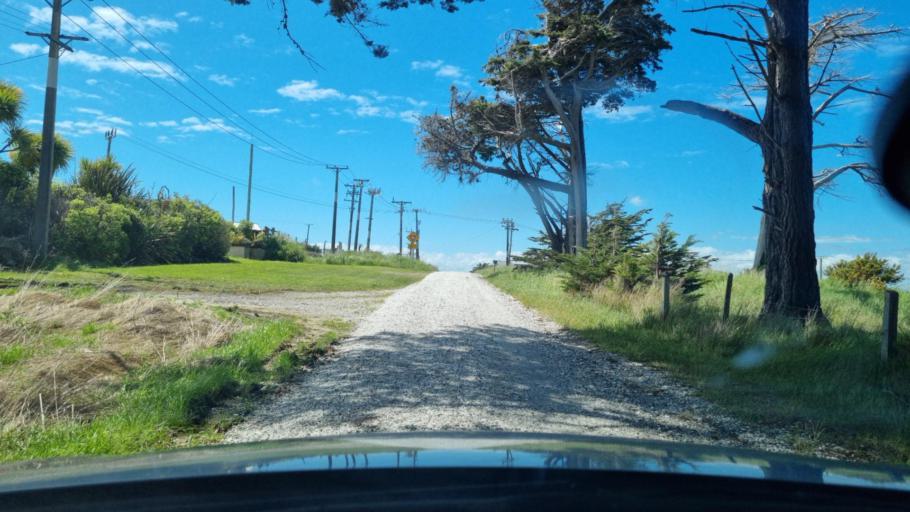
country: NZ
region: Southland
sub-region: Invercargill City
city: Bluff
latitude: -46.5857
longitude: 168.3035
